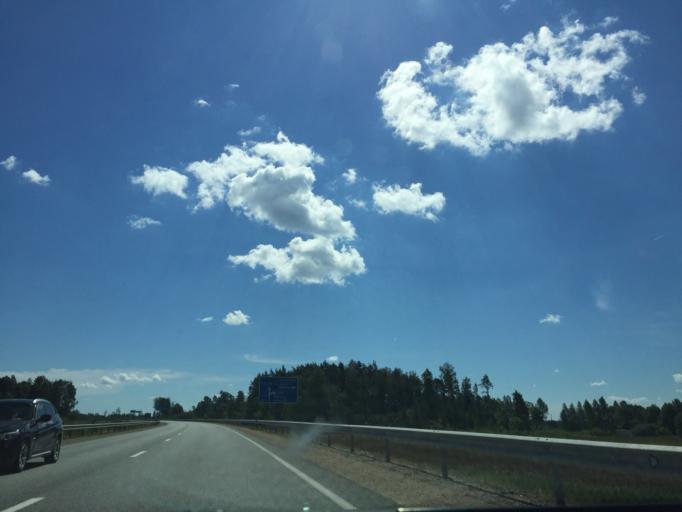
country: LV
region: Koknese
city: Koknese
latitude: 56.6685
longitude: 25.4077
